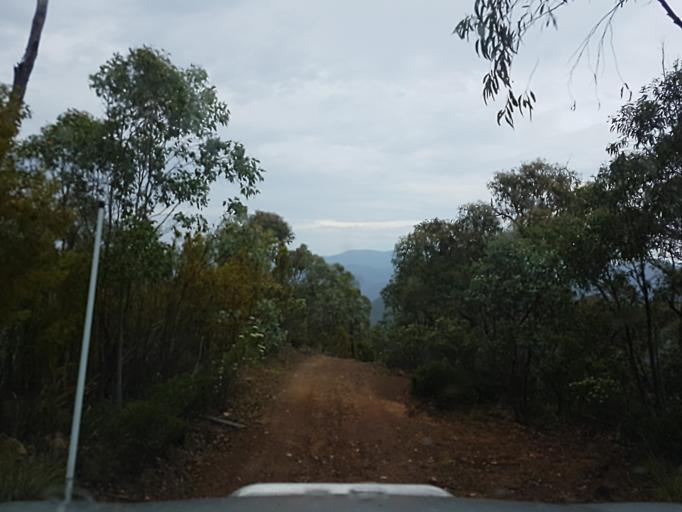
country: AU
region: New South Wales
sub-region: Snowy River
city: Jindabyne
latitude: -36.9245
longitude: 148.3526
